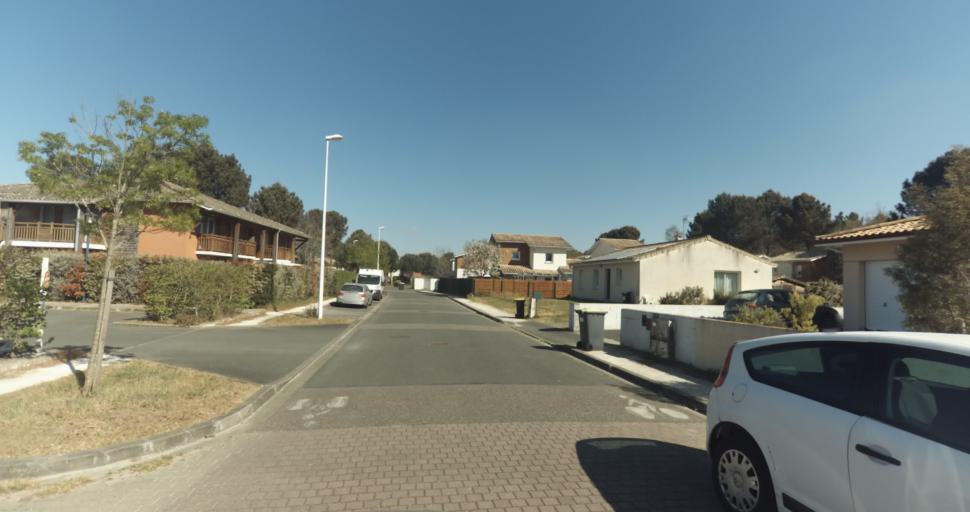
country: FR
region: Aquitaine
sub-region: Departement de la Gironde
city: Martignas-sur-Jalle
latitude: 44.8013
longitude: -0.7774
